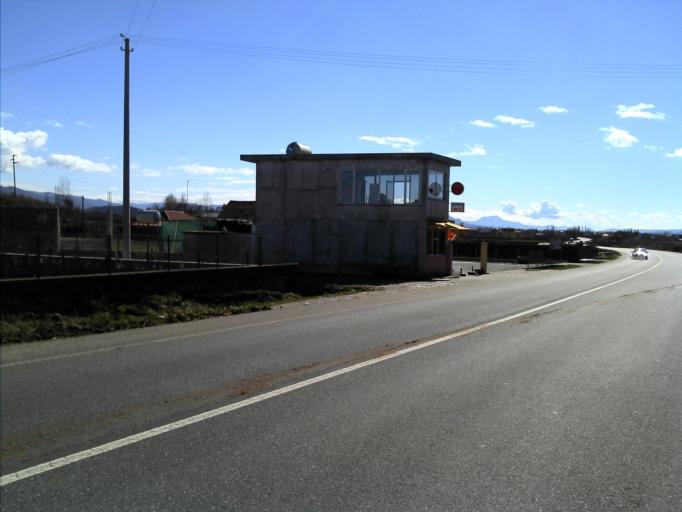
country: AL
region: Shkoder
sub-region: Rrethi i Malesia e Madhe
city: Koplik
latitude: 42.1840
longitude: 19.4592
